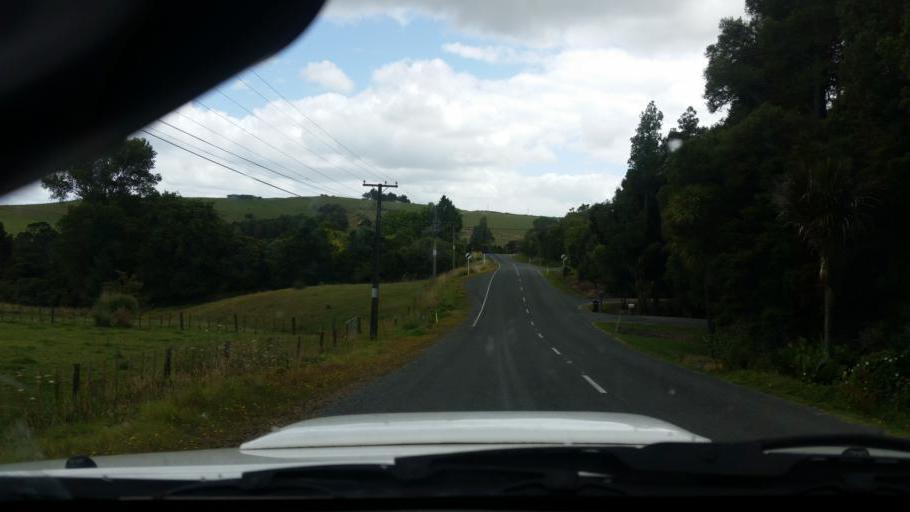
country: NZ
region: Northland
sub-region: Whangarei
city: Ruakaka
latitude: -36.0984
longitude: 174.3508
